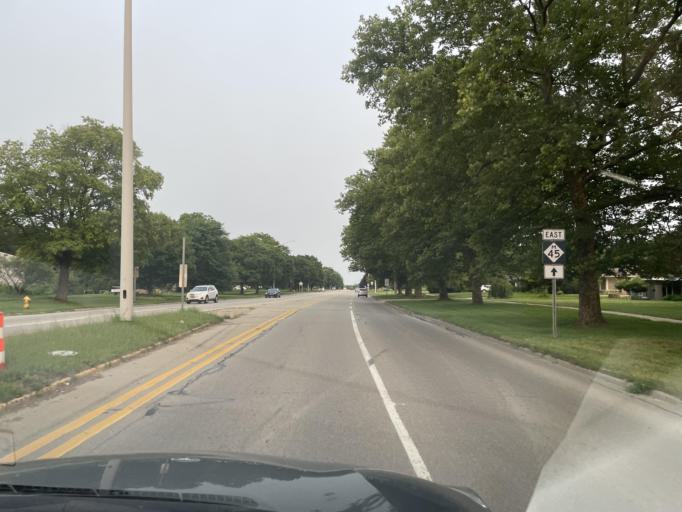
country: US
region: Michigan
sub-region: Kent County
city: Grand Rapids
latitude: 42.9710
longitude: -85.7166
